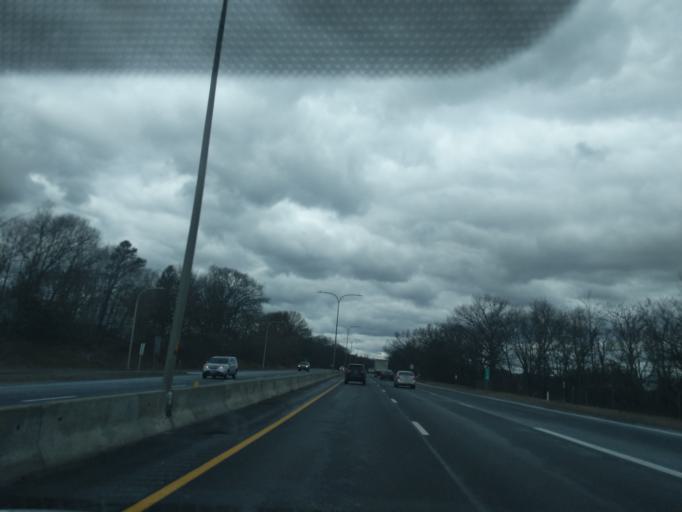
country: US
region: Rhode Island
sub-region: Providence County
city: Providence
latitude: 41.8552
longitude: -71.4275
